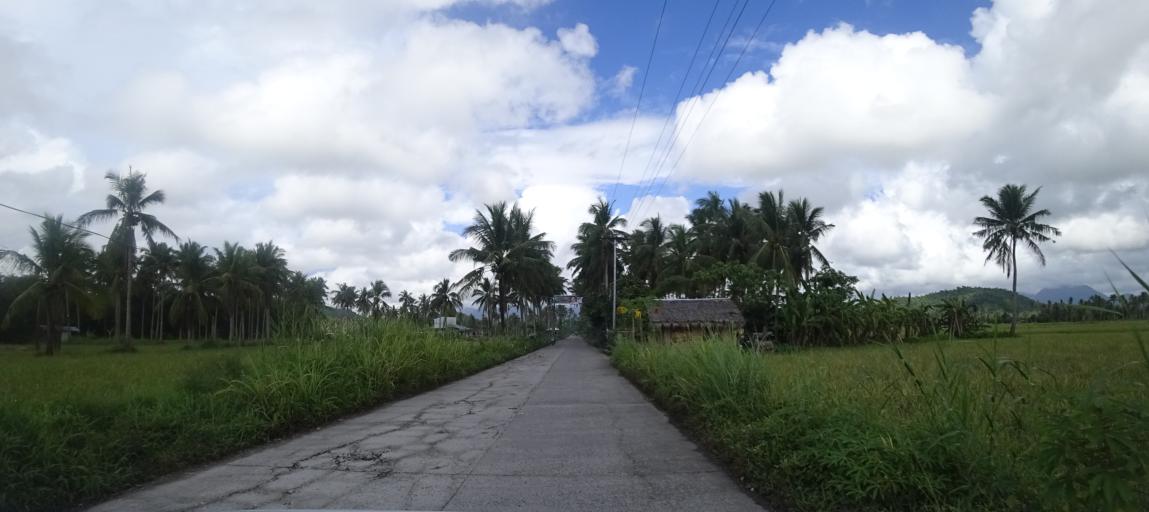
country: PH
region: Eastern Visayas
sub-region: Province of Leyte
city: MacArthur
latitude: 10.8170
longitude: 124.9763
